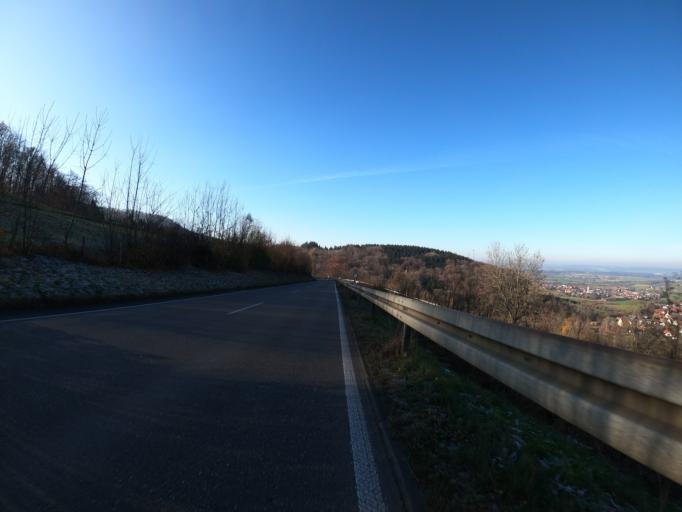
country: DE
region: Baden-Wuerttemberg
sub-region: Regierungsbezirk Stuttgart
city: Gammelshausen
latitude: 48.6331
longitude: 9.6545
